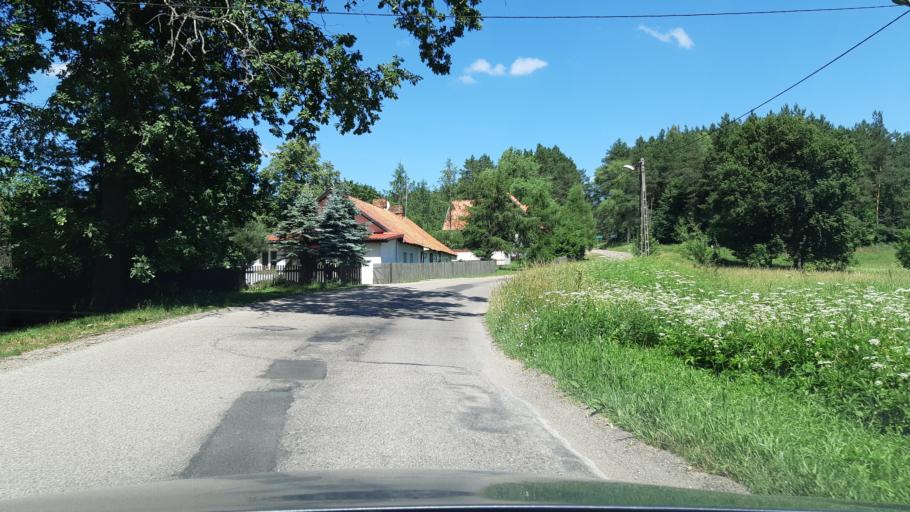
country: PL
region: Warmian-Masurian Voivodeship
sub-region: Powiat mragowski
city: Mikolajki
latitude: 53.7383
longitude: 21.5025
